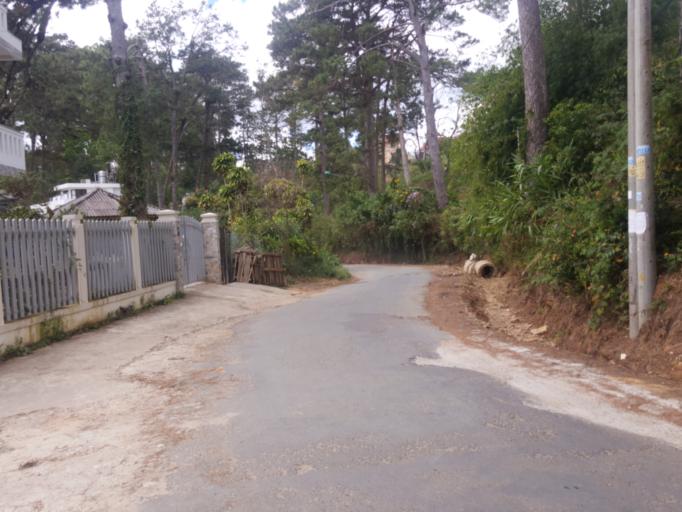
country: VN
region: Lam Dong
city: Da Lat
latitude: 11.9465
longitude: 108.4392
